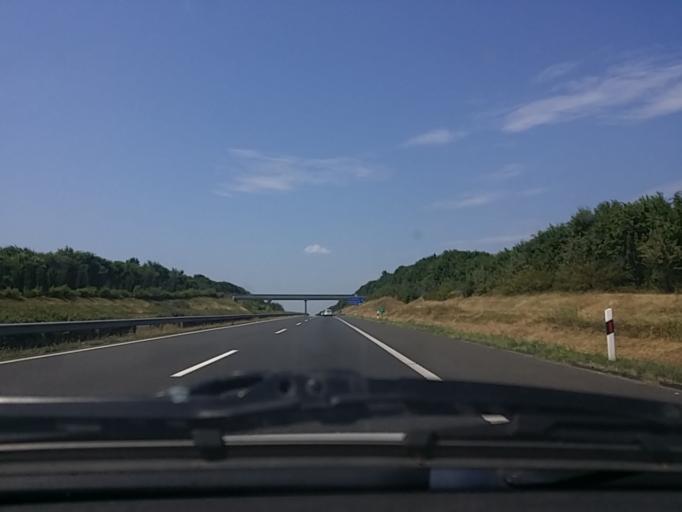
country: HU
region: Somogy
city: Balatonlelle
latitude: 46.7643
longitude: 17.6830
